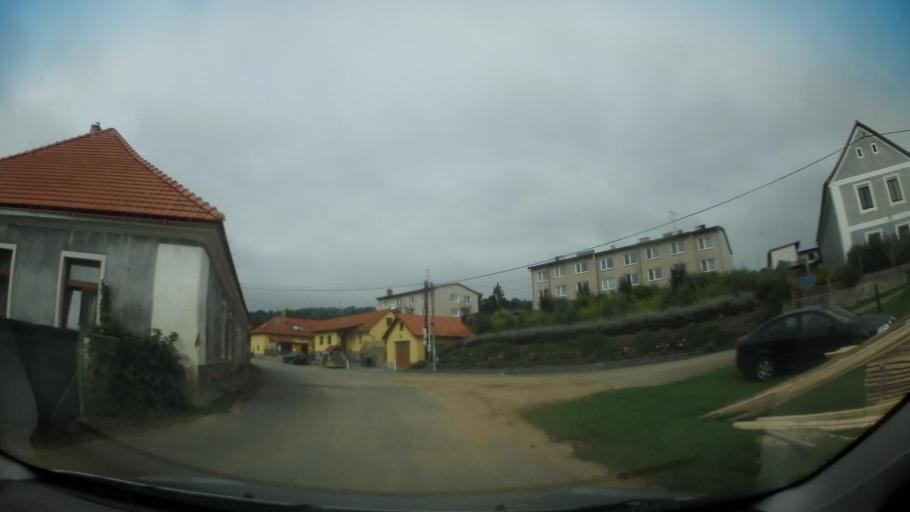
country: CZ
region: Central Bohemia
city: Sedlcany
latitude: 49.7154
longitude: 14.4137
